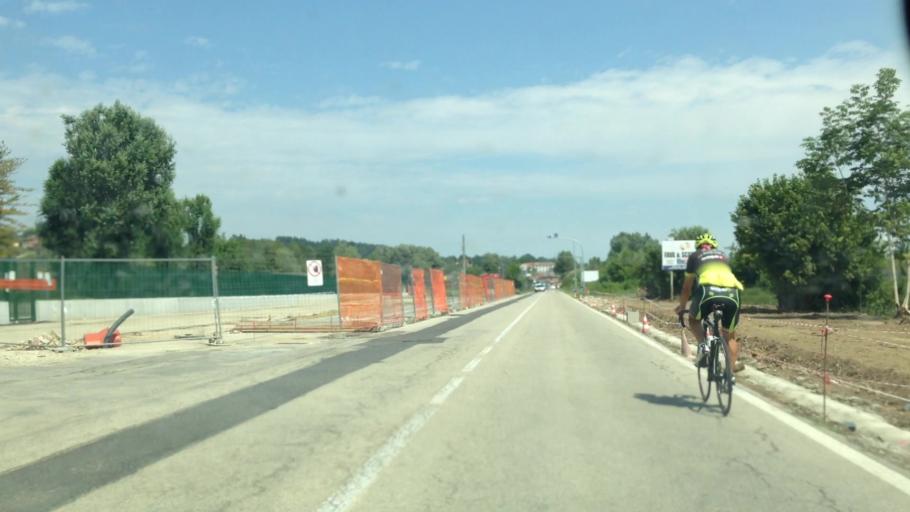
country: IT
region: Piedmont
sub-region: Provincia di Asti
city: Portacomaro
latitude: 44.9495
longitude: 8.2236
